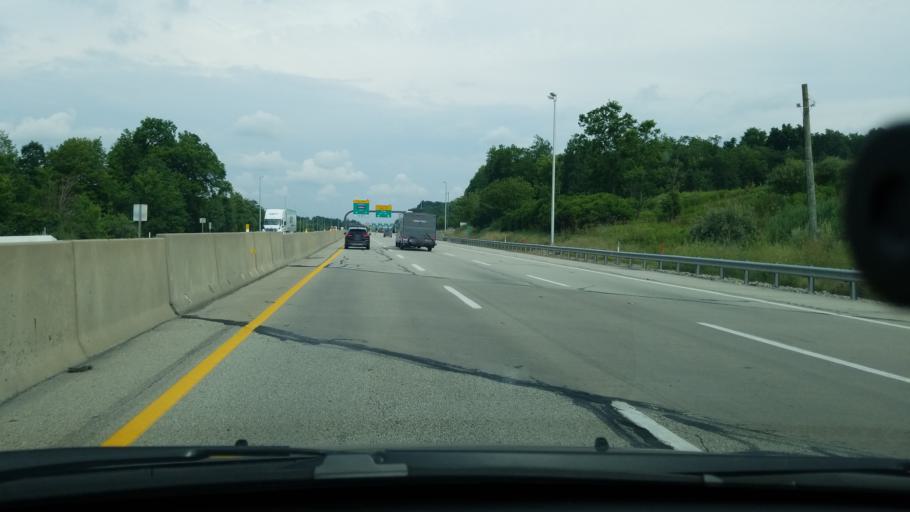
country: US
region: Pennsylvania
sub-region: Lawrence County
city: Bessemer
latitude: 40.9055
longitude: -80.5016
